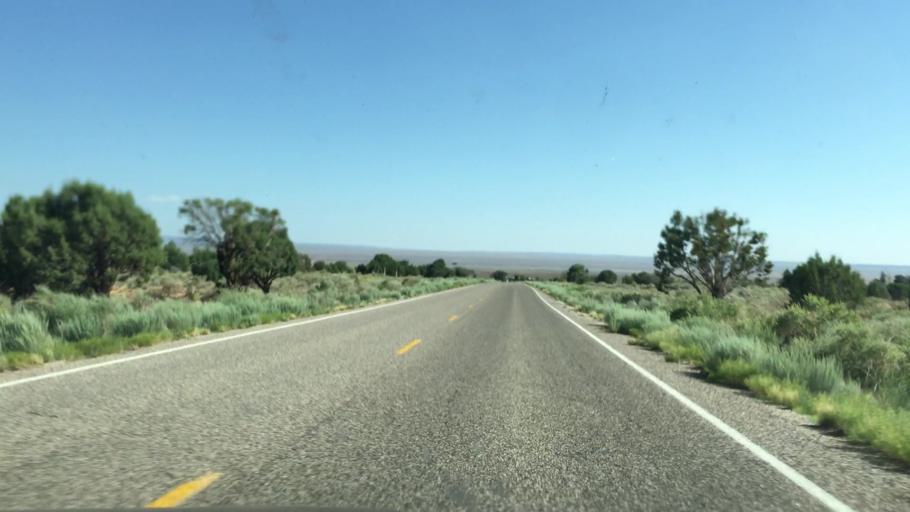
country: US
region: Arizona
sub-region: Coconino County
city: Fredonia
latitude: 36.8683
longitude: -112.7376
